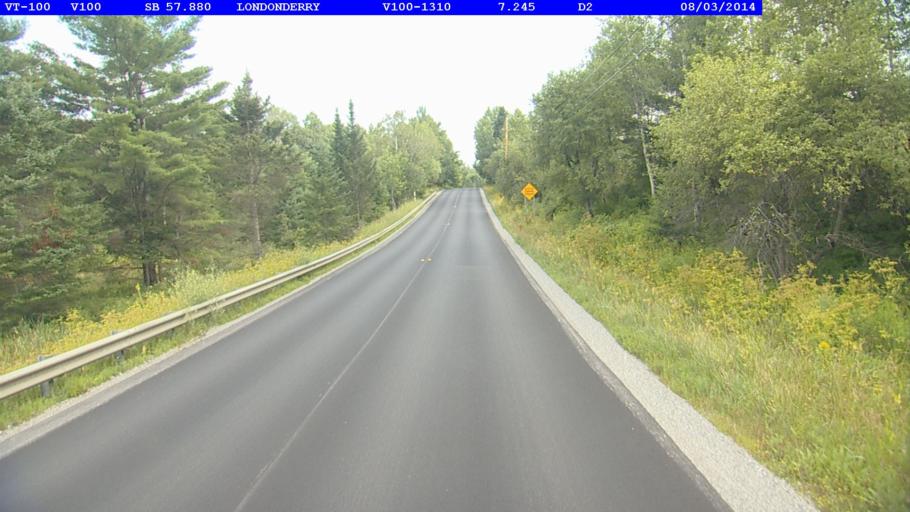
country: US
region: Vermont
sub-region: Windsor County
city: Chester
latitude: 43.2440
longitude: -72.7959
